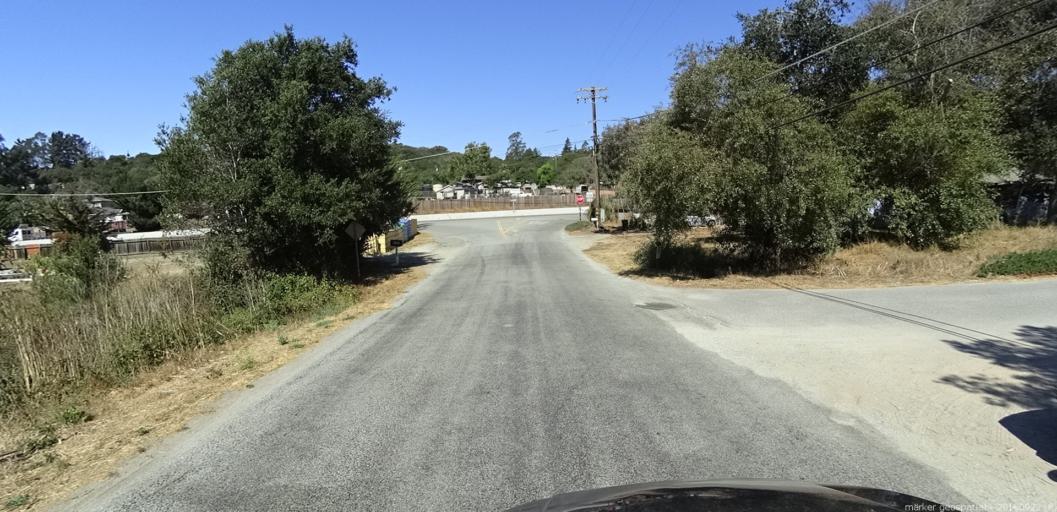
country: US
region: California
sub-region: Monterey County
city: Prunedale
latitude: 36.8134
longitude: -121.6406
